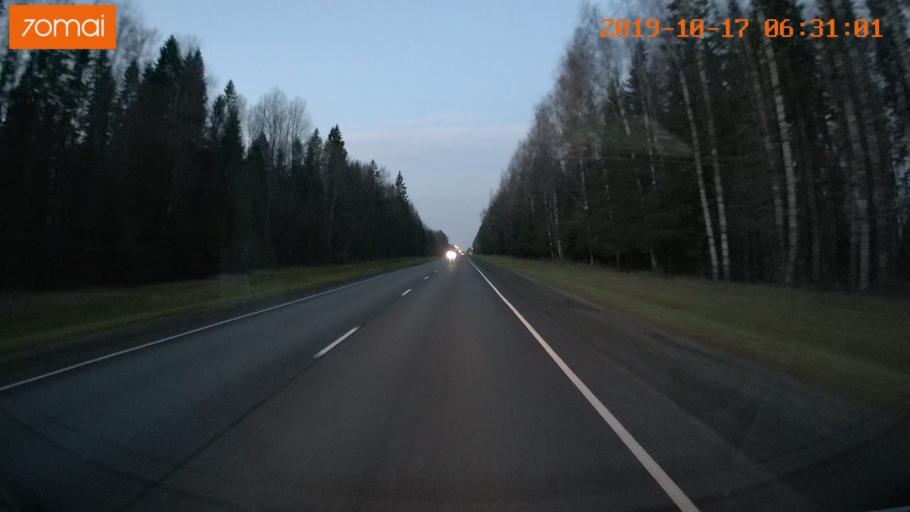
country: RU
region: Ivanovo
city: Lezhnevo
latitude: 56.7313
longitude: 40.7071
